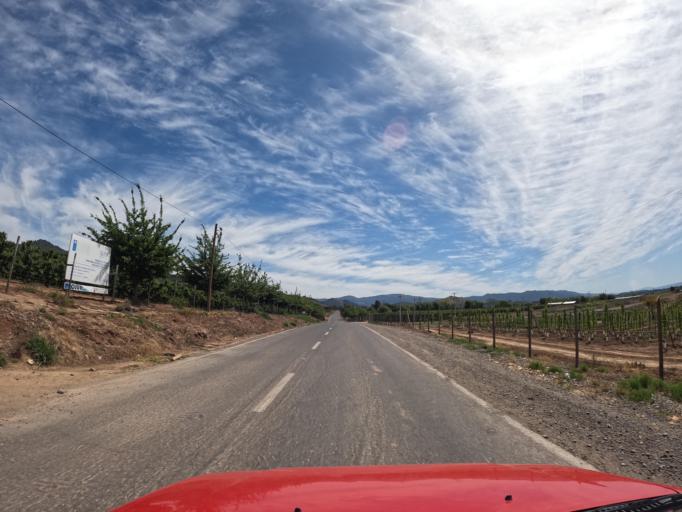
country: CL
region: Maule
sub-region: Provincia de Talca
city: Talca
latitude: -35.1218
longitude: -71.6629
